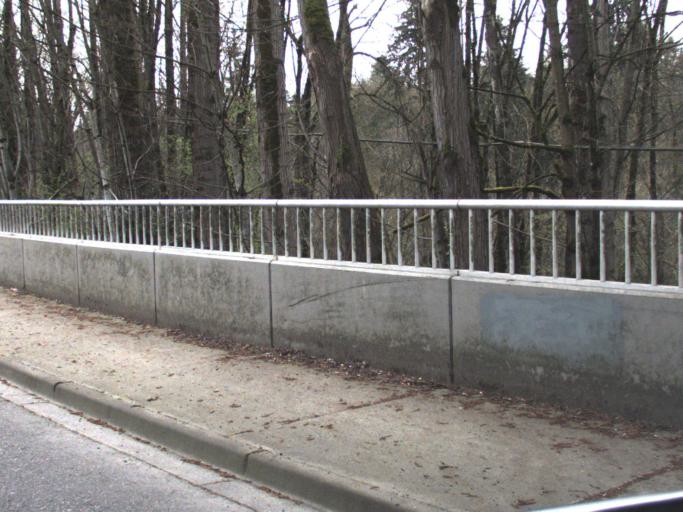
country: US
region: Washington
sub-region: King County
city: Kent
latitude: 47.3813
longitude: -122.2193
